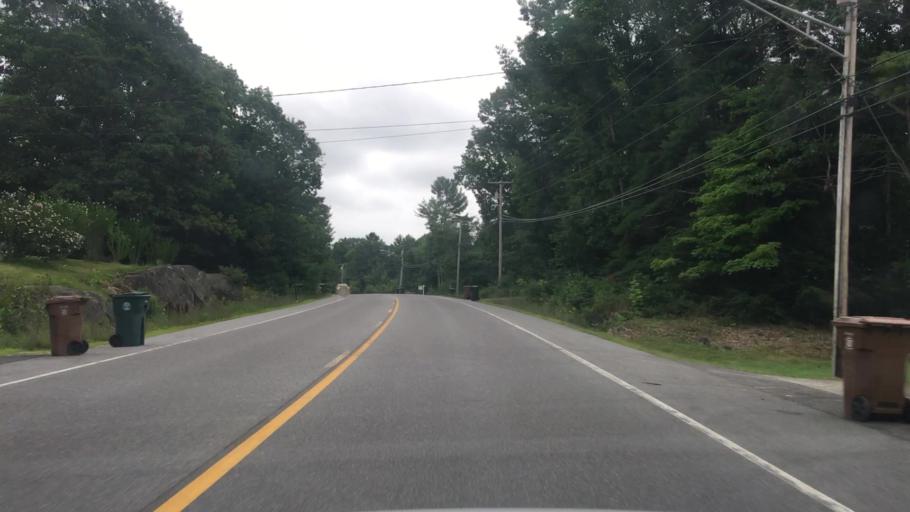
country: US
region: Maine
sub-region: York County
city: Biddeford
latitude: 43.5276
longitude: -70.5001
